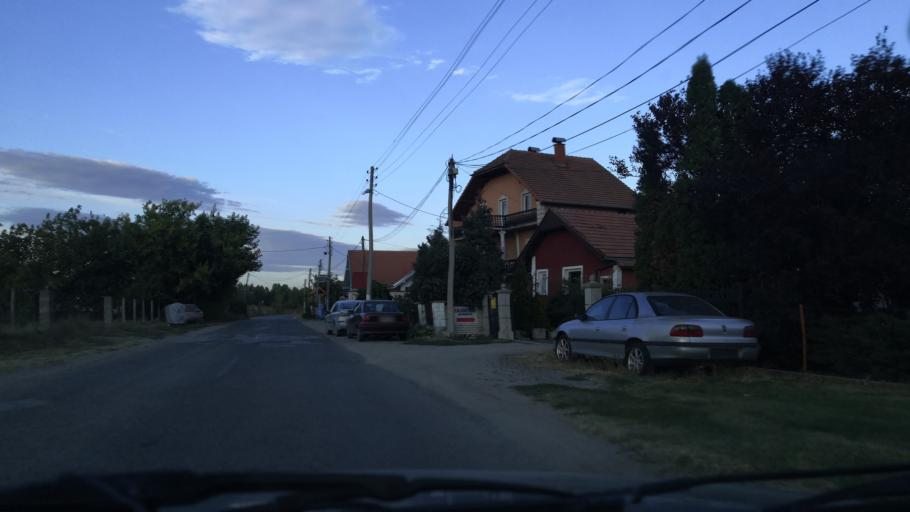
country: RS
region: Central Serbia
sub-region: Borski Okrug
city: Negotin
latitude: 44.2374
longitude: 22.5491
